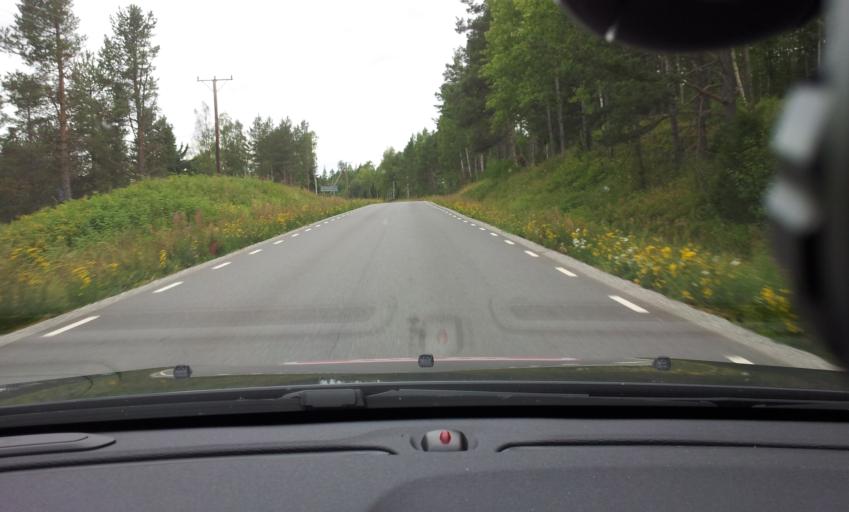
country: SE
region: Jaemtland
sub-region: Braecke Kommun
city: Braecke
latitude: 63.0769
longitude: 15.3833
